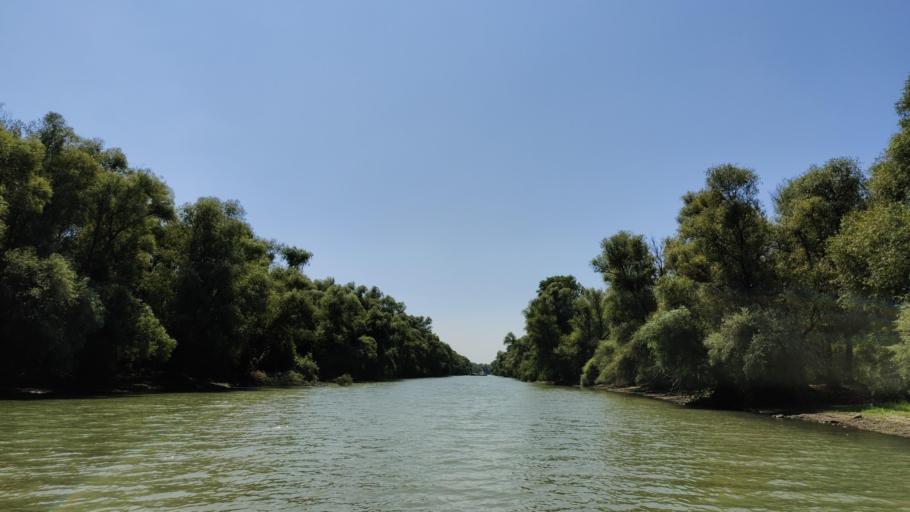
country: RO
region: Tulcea
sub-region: Comuna Pardina
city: Pardina
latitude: 45.2491
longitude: 28.9241
